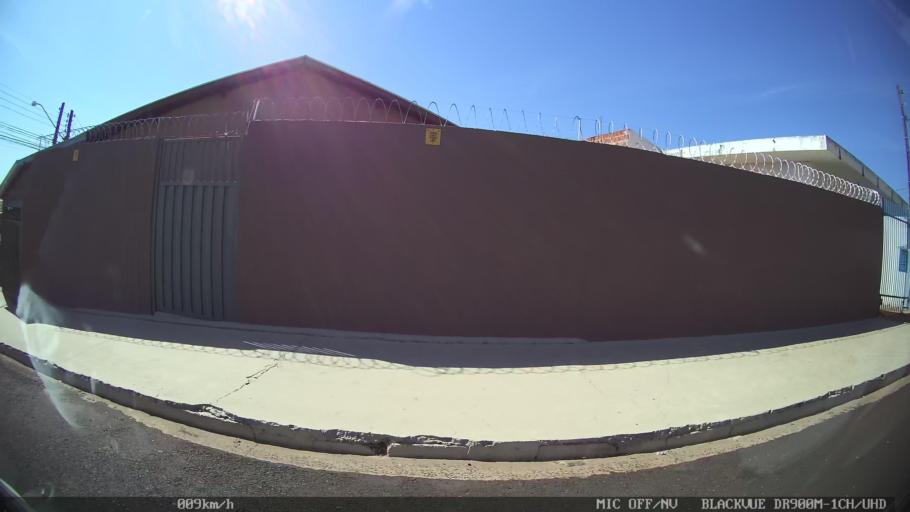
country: BR
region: Sao Paulo
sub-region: Sao Jose Do Rio Preto
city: Sao Jose do Rio Preto
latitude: -20.7746
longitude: -49.4031
